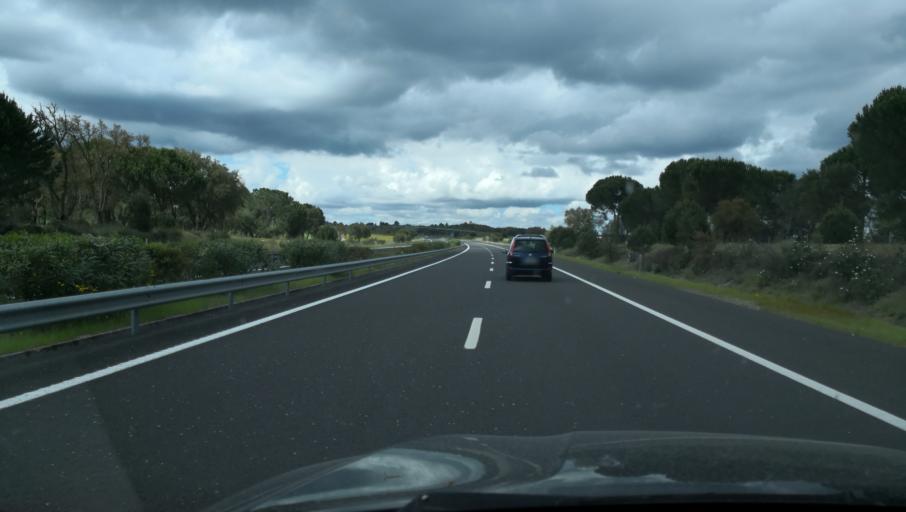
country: PT
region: Evora
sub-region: Vendas Novas
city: Vendas Novas
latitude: 38.7018
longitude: -8.6411
